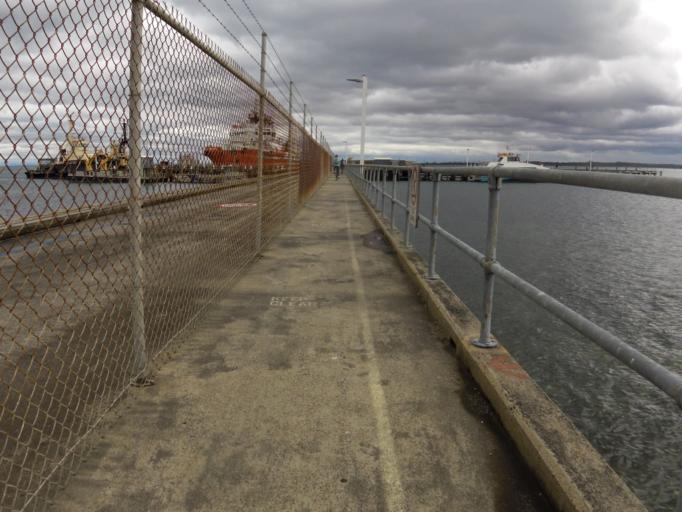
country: AU
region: Victoria
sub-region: Mornington Peninsula
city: Crib Point
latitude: -38.3730
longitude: 145.2236
